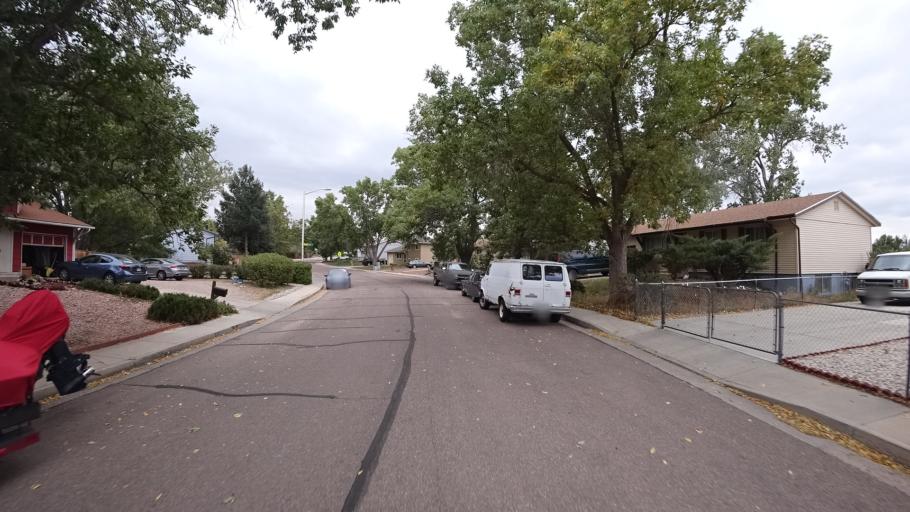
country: US
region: Colorado
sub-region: El Paso County
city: Cimarron Hills
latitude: 38.8913
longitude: -104.7433
